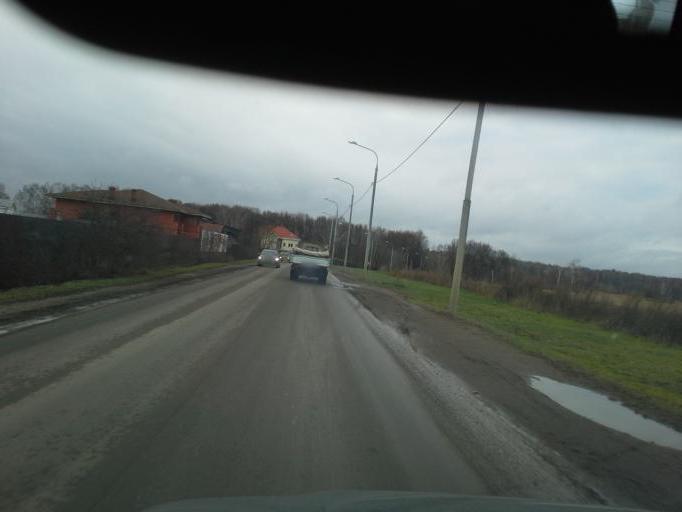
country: RU
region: Moskovskaya
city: Filimonki
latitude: 55.5630
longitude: 37.4138
